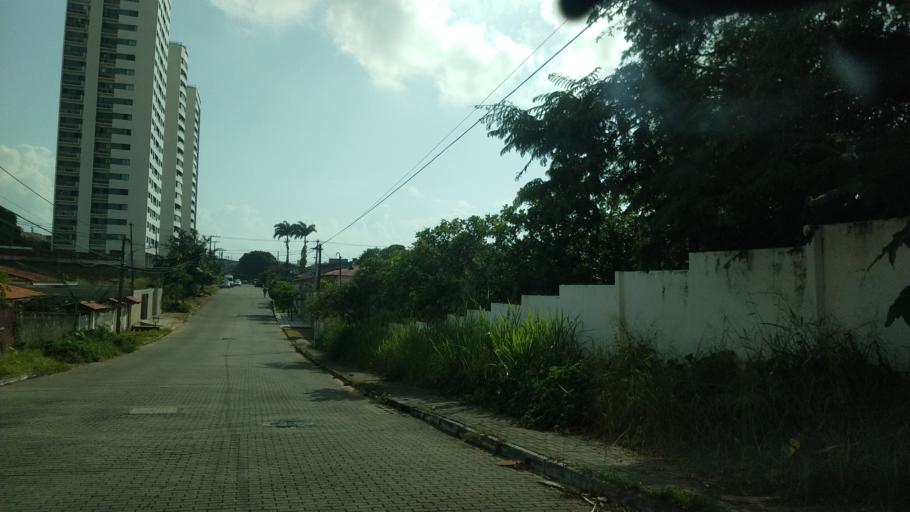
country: BR
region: Rio Grande do Norte
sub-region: Natal
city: Natal
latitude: -5.8574
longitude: -35.2017
